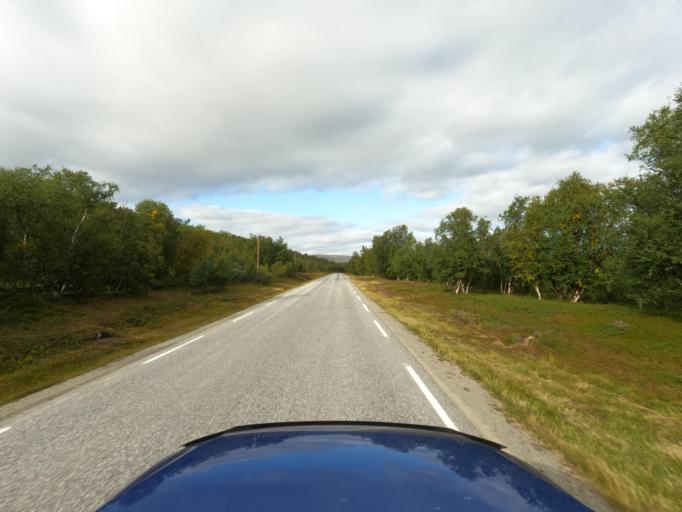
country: NO
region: Finnmark Fylke
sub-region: Porsanger
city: Lakselv
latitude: 70.1435
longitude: 24.9076
